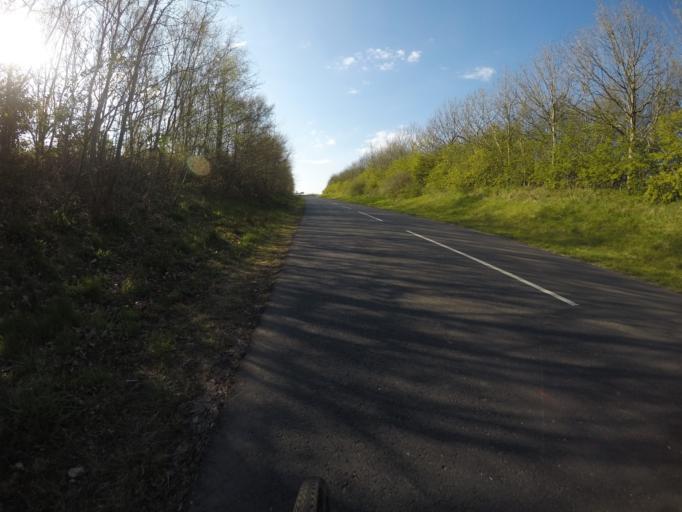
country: GB
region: Scotland
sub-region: North Ayrshire
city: Stevenston
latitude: 55.6509
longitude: -4.7396
